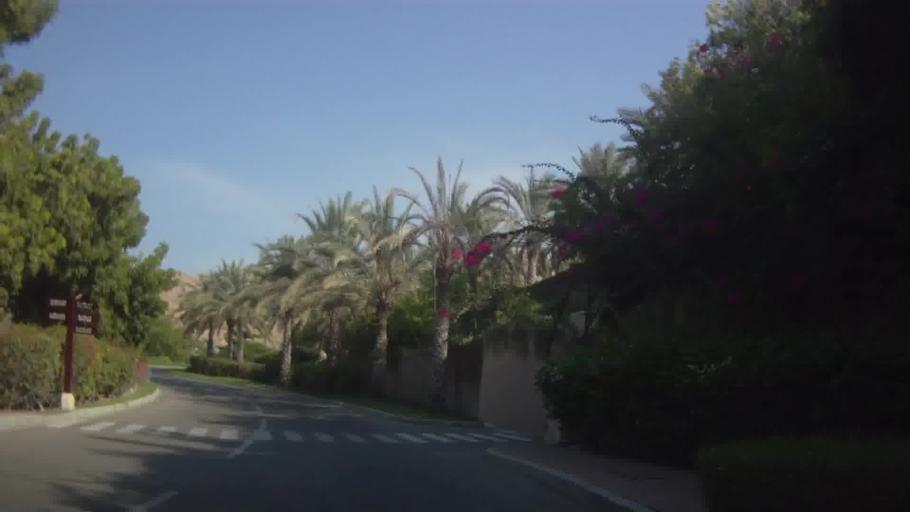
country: OM
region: Muhafazat Masqat
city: Muscat
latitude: 23.5494
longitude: 58.6595
